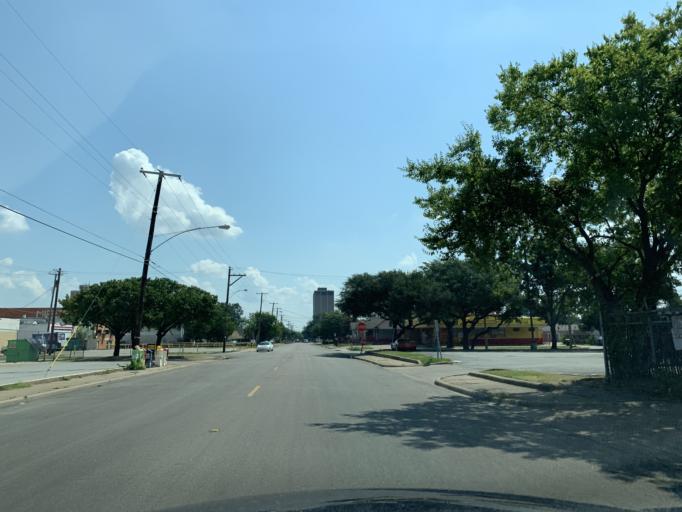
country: US
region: Texas
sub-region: Dallas County
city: Dallas
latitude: 32.7422
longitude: -96.8309
